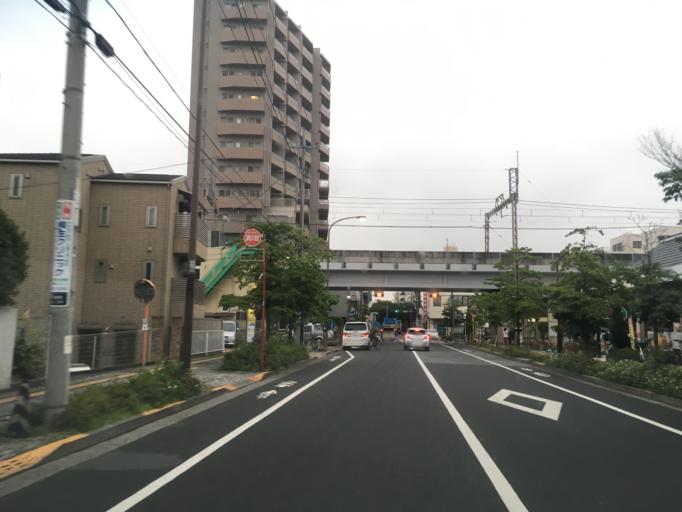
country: JP
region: Tokyo
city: Chofugaoka
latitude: 35.6454
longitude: 139.5368
